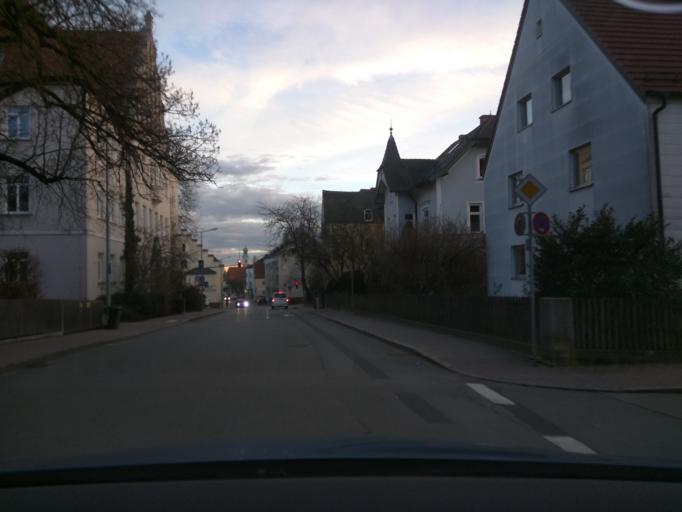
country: DE
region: Bavaria
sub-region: Upper Bavaria
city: Freising
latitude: 48.4038
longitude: 11.7396
